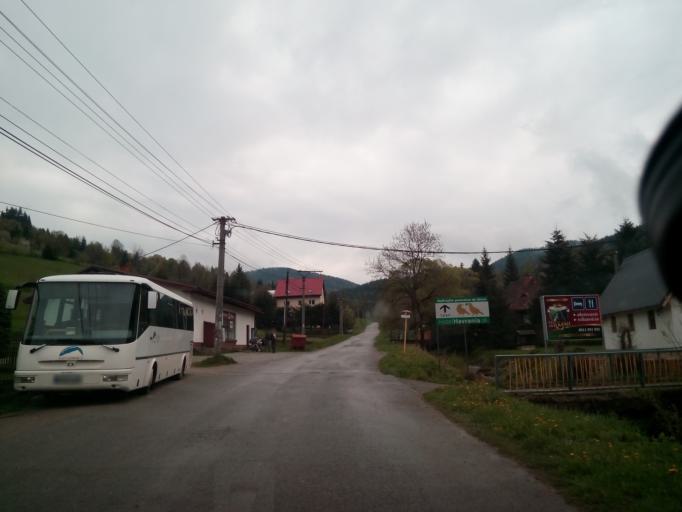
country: SK
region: Zilinsky
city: Oravska Lesna
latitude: 49.2978
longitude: 19.1855
